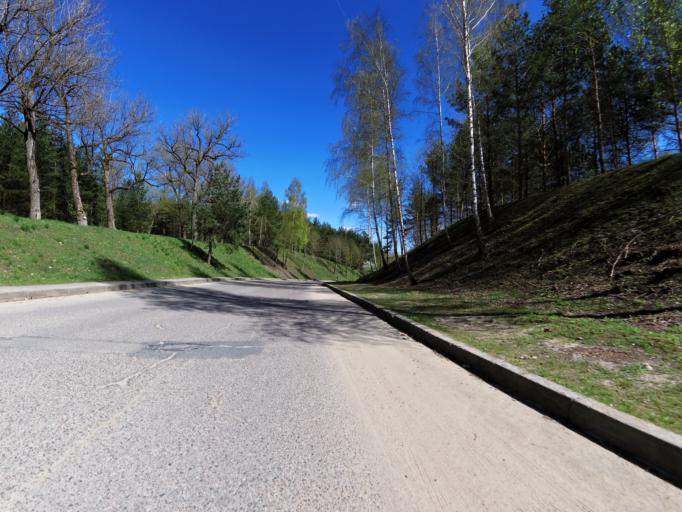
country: LT
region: Vilnius County
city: Rasos
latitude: 54.6885
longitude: 25.3135
